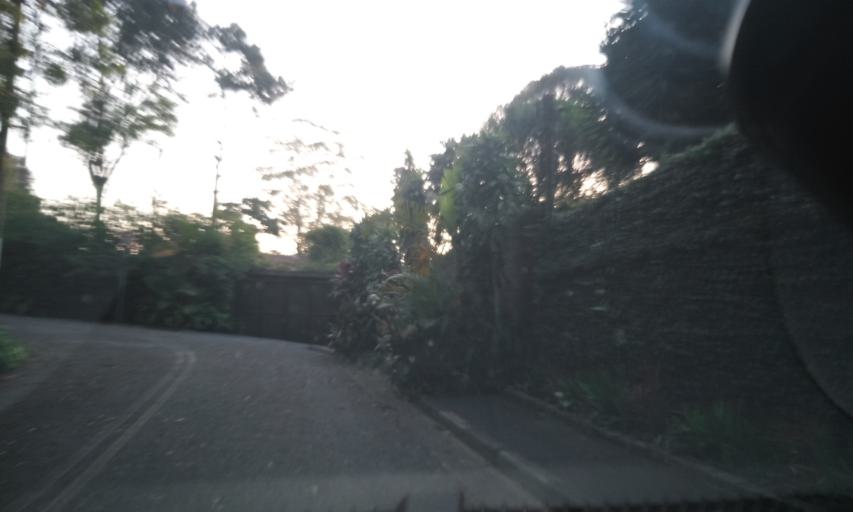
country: BR
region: Sao Paulo
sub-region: Sao Bernardo Do Campo
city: Sao Bernardo do Campo
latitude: -23.7925
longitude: -46.5440
